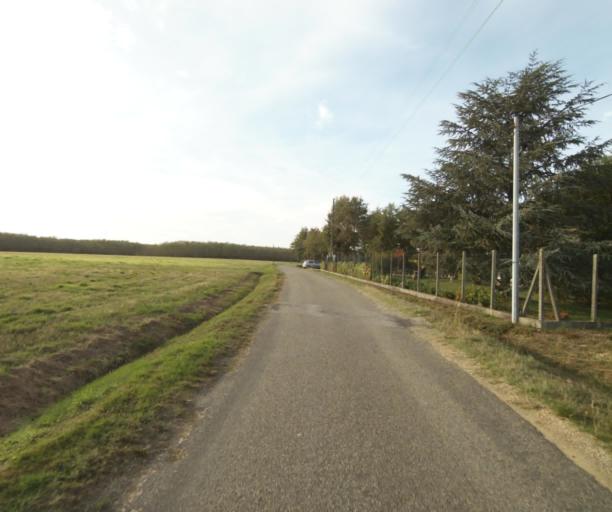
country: FR
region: Midi-Pyrenees
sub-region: Departement du Tarn-et-Garonne
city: Campsas
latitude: 43.8721
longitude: 1.3328
